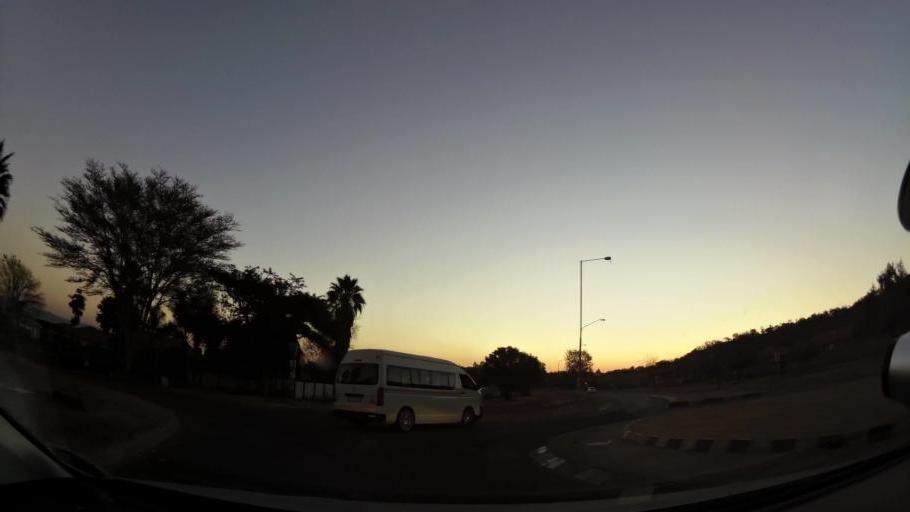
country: ZA
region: Gauteng
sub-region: City of Tshwane Metropolitan Municipality
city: Pretoria
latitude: -25.7315
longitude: 28.1388
